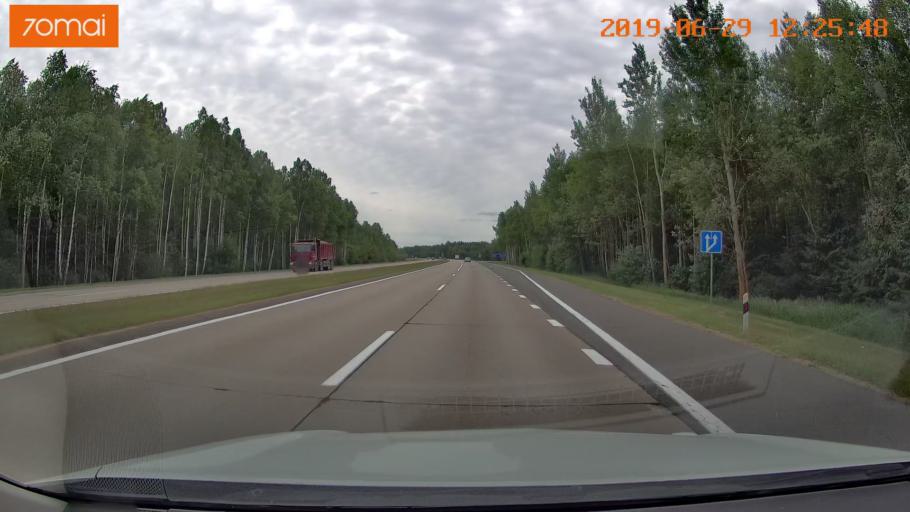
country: BY
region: Minsk
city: Uzda
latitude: 53.4707
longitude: 27.4628
